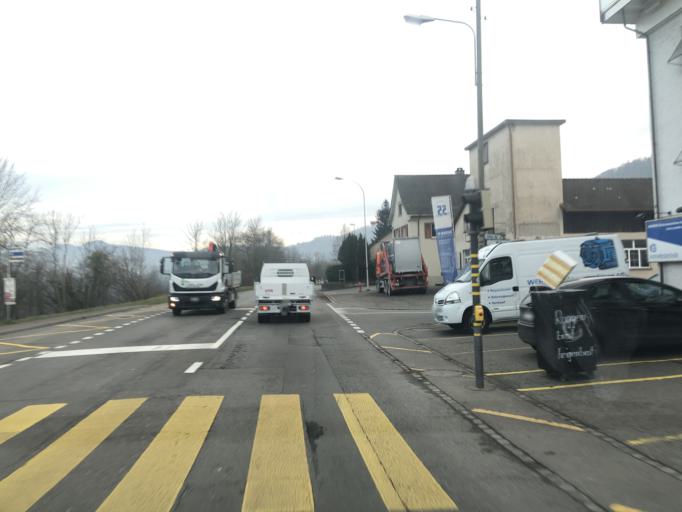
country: CH
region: Aargau
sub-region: Bezirk Baden
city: Turgi
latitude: 47.4886
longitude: 8.2611
